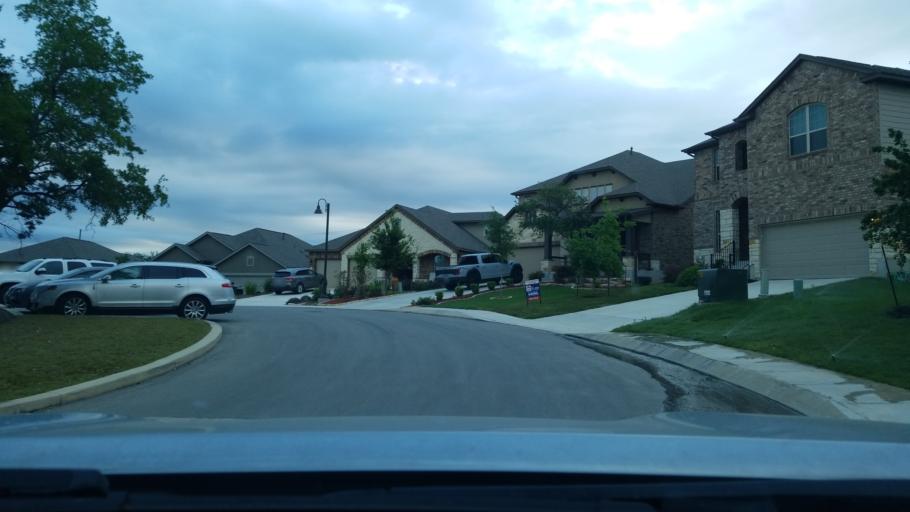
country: US
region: Texas
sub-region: Bexar County
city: Timberwood Park
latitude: 29.7162
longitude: -98.4555
